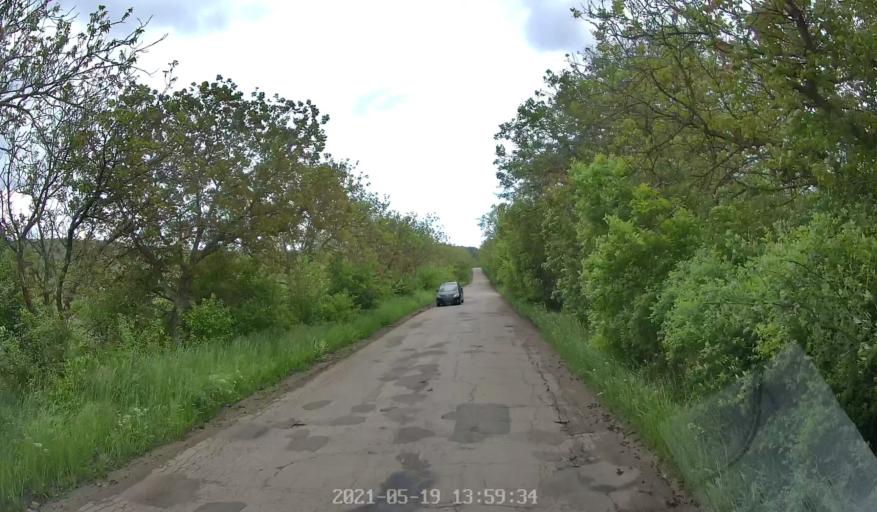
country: MD
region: Chisinau
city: Chisinau
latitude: 47.0397
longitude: 28.9246
